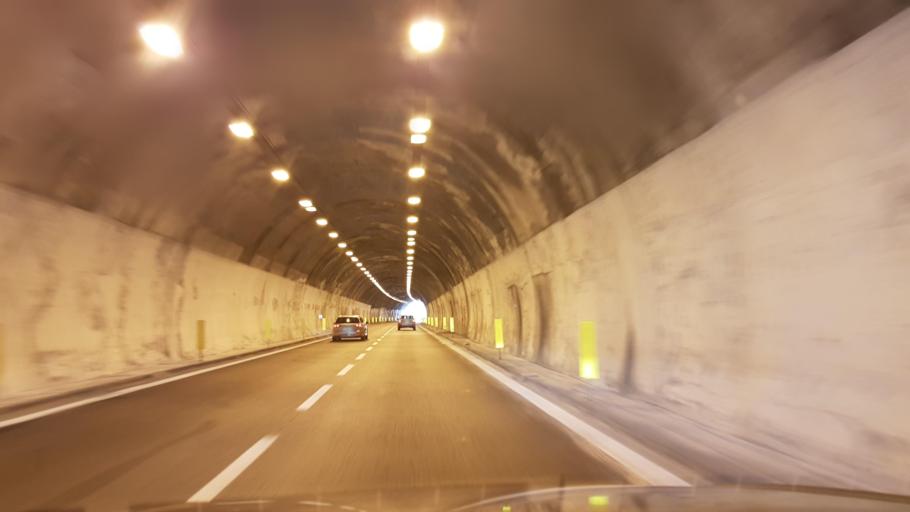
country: IT
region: Liguria
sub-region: Provincia di Imperia
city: Diano Marina
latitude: 43.9124
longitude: 8.0685
